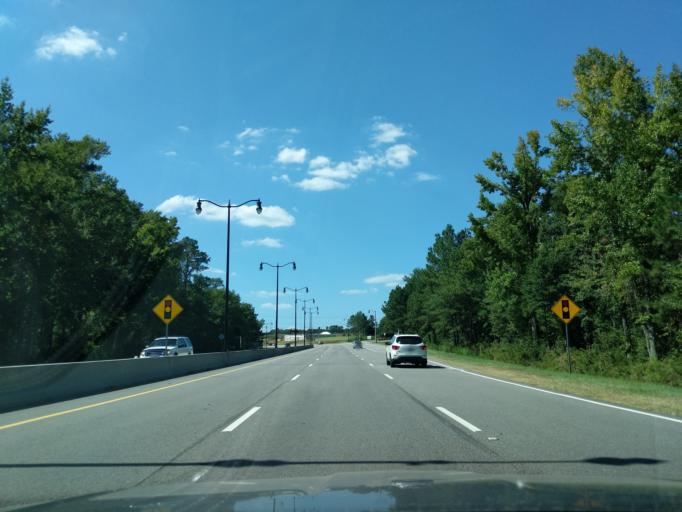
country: US
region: South Carolina
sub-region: Aiken County
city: North Augusta
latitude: 33.5205
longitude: -82.0165
